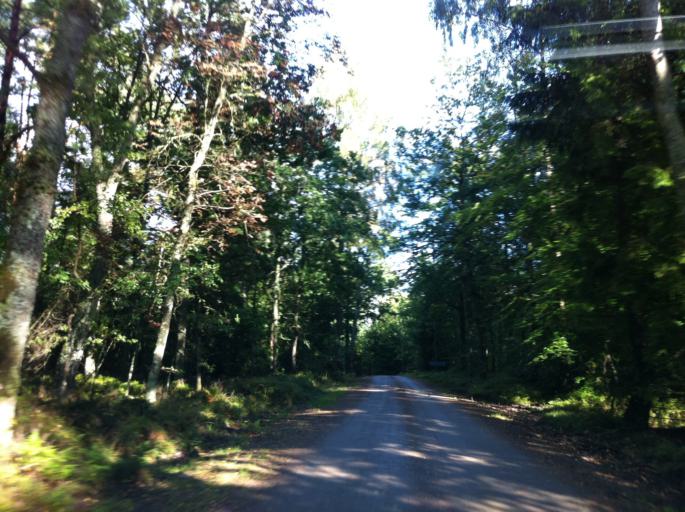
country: SE
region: Skane
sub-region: Hassleholms Kommun
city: Sosdala
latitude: 56.1333
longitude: 13.5577
